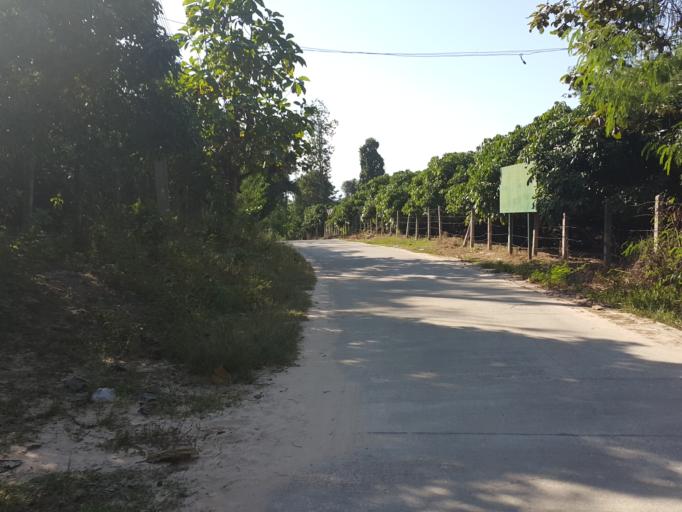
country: TH
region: Chiang Mai
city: Mae On
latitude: 18.7956
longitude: 99.1832
